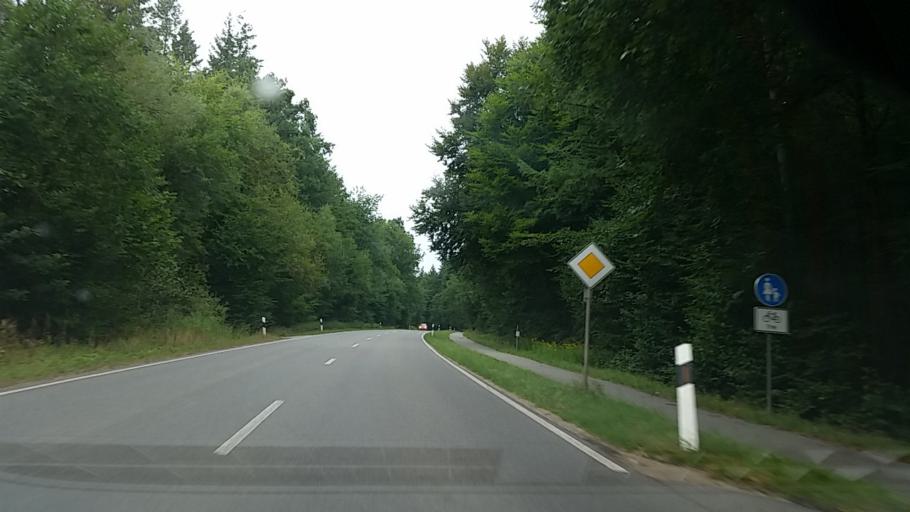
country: DE
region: Schleswig-Holstein
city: Dassendorf
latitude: 53.5139
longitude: 10.3560
